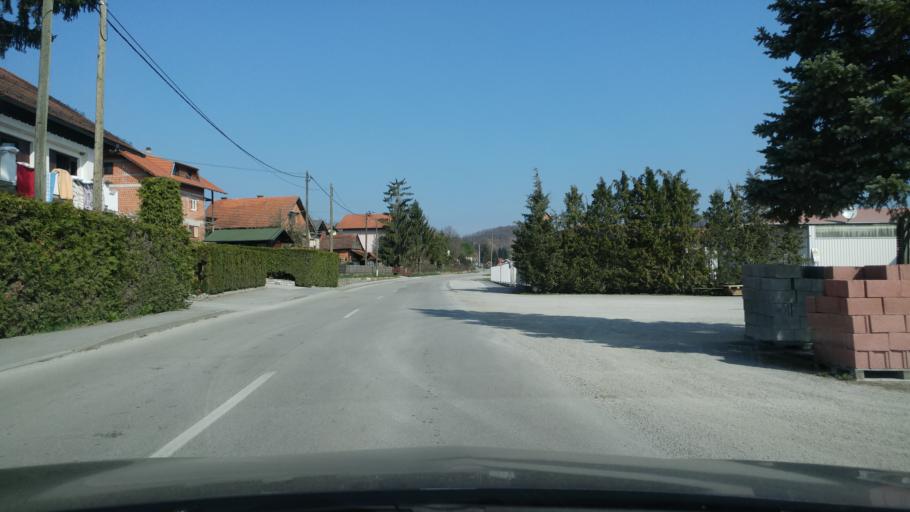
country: HR
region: Zagrebacka
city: Pojatno
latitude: 45.9264
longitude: 15.7721
